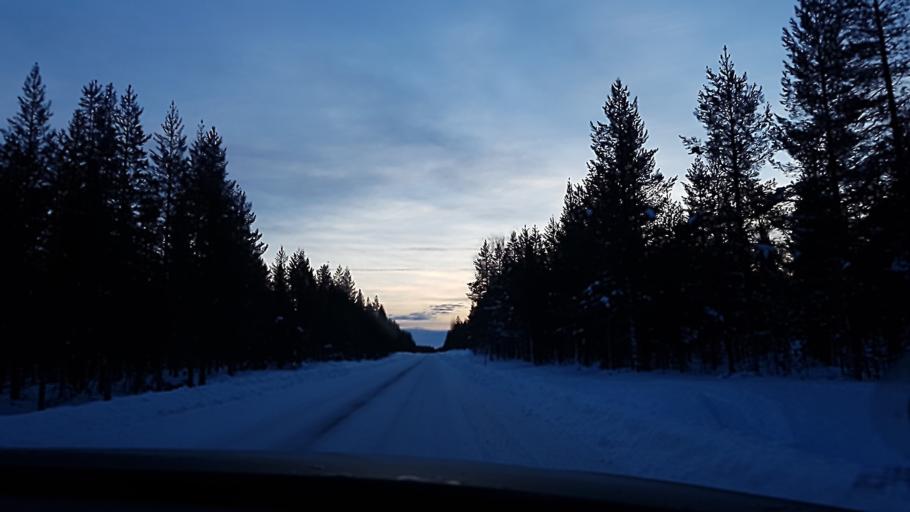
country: SE
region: Norrbotten
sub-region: Arvidsjaurs Kommun
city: Arvidsjaur
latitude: 65.9173
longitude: 19.4592
